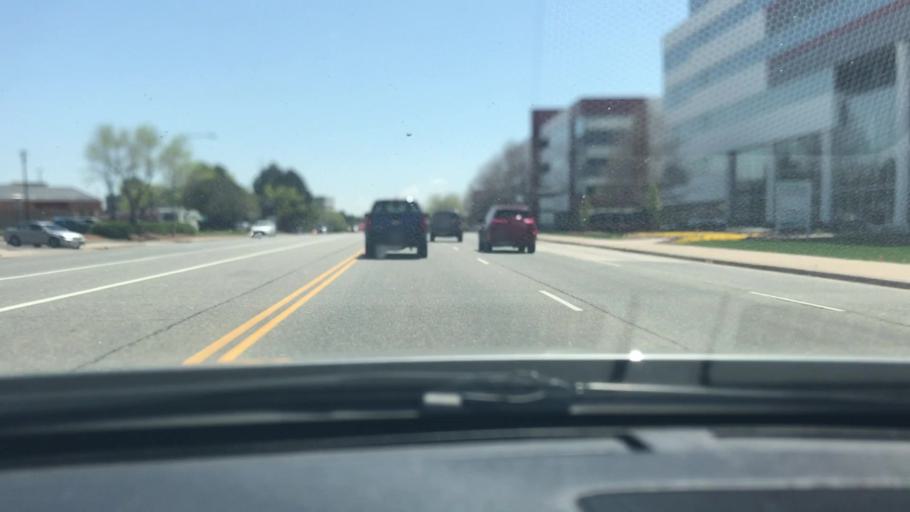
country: US
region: Colorado
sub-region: Adams County
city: Aurora
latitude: 39.6740
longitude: -104.8701
